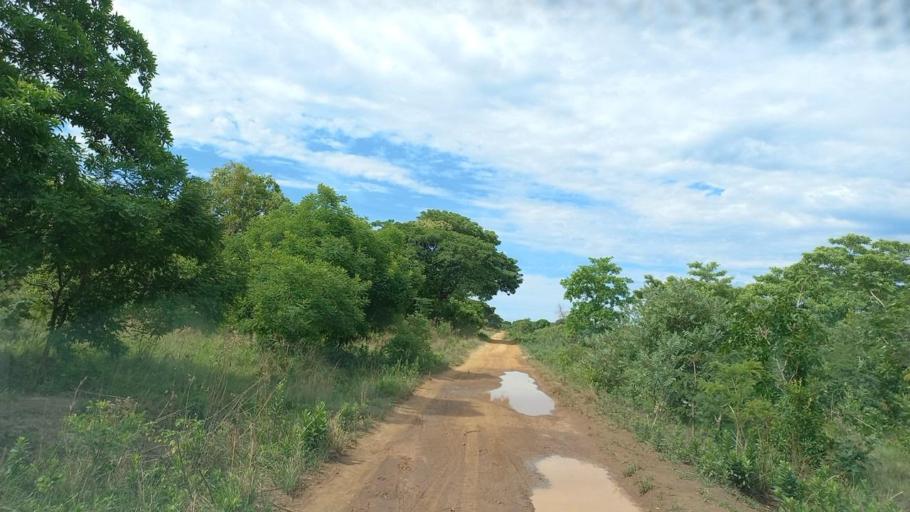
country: ZM
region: North-Western
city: Kabompo
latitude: -13.5107
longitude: 24.3939
